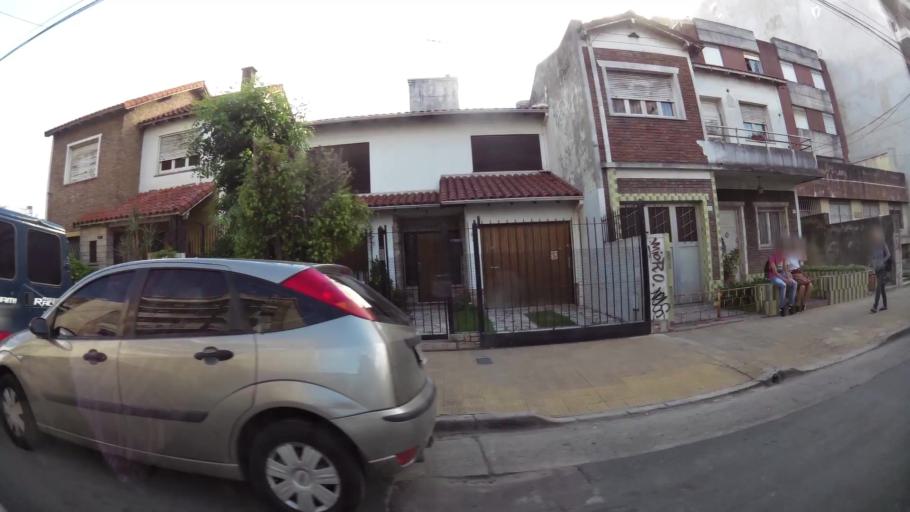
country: AR
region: Buenos Aires
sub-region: Partido de General San Martin
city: General San Martin
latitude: -34.5487
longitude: -58.5567
